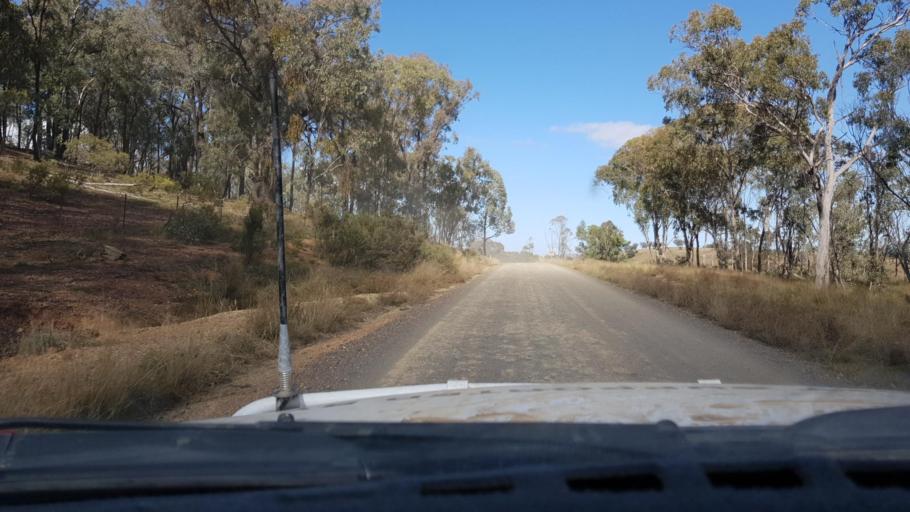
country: AU
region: New South Wales
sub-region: Tamworth Municipality
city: Manilla
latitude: -30.4652
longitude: 150.7435
